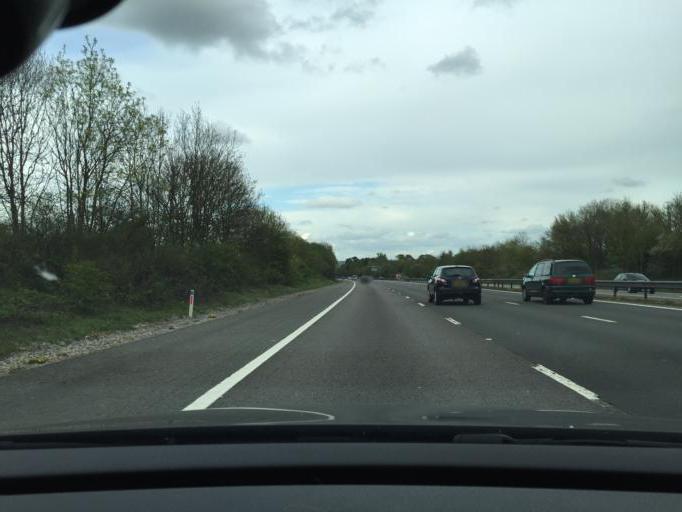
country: GB
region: England
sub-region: West Berkshire
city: Basildon
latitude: 51.4600
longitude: -1.1380
